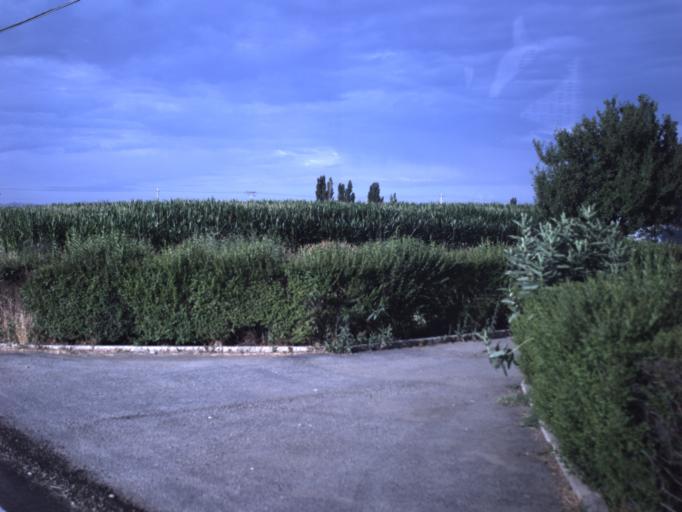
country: US
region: Utah
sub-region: Weber County
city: Plain City
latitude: 41.2482
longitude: -112.0926
